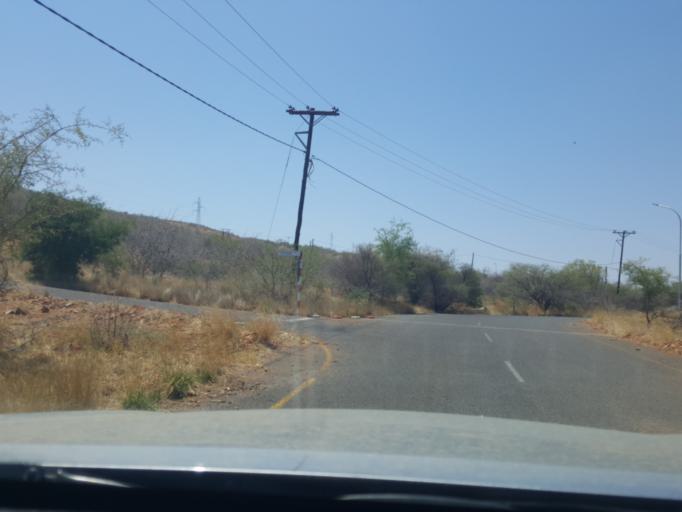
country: BW
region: South East
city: Lobatse
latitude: -25.1890
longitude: 25.6768
